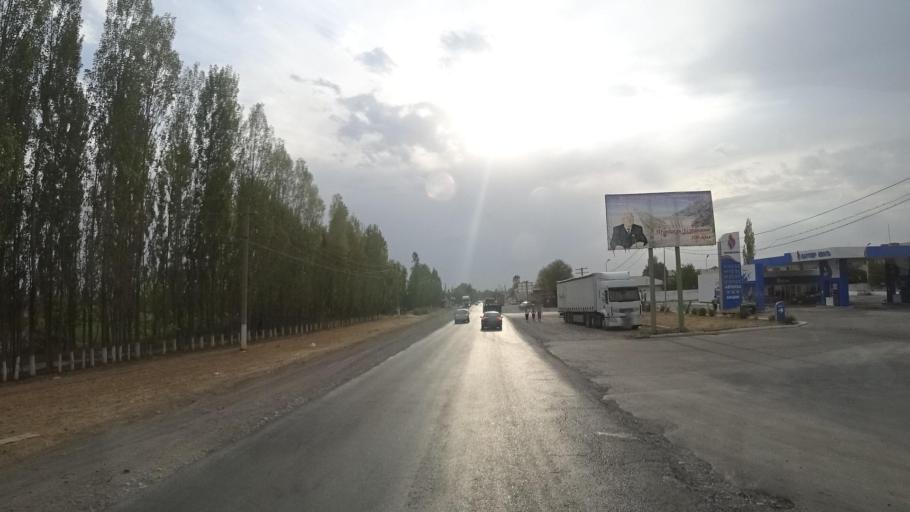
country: KG
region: Jalal-Abad
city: Massy
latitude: 41.0645
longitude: 72.6499
